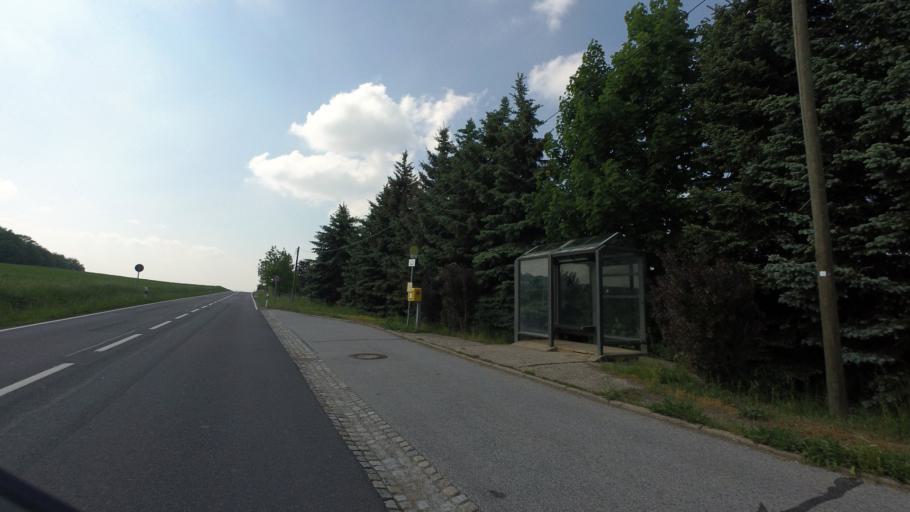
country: DE
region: Saxony
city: Weissenberg
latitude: 51.1877
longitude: 14.6377
